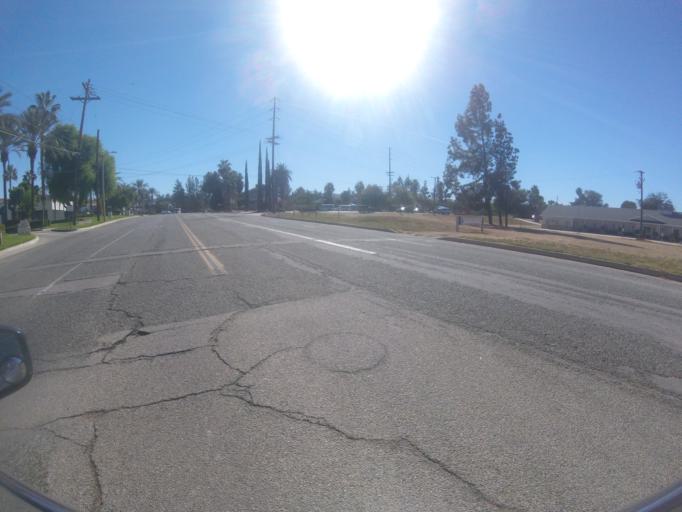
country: US
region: California
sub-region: San Bernardino County
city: Redlands
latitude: 34.0490
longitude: -117.2087
